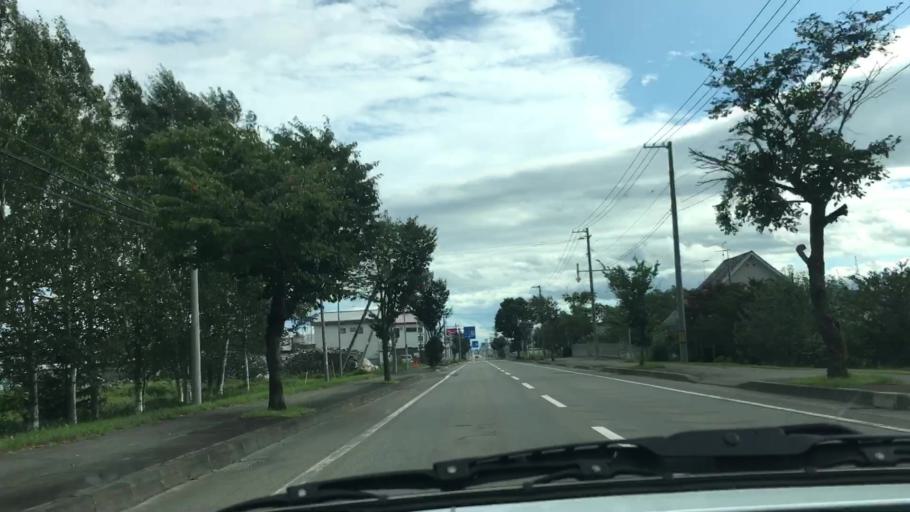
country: JP
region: Hokkaido
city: Otofuke
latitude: 43.2386
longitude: 143.2964
